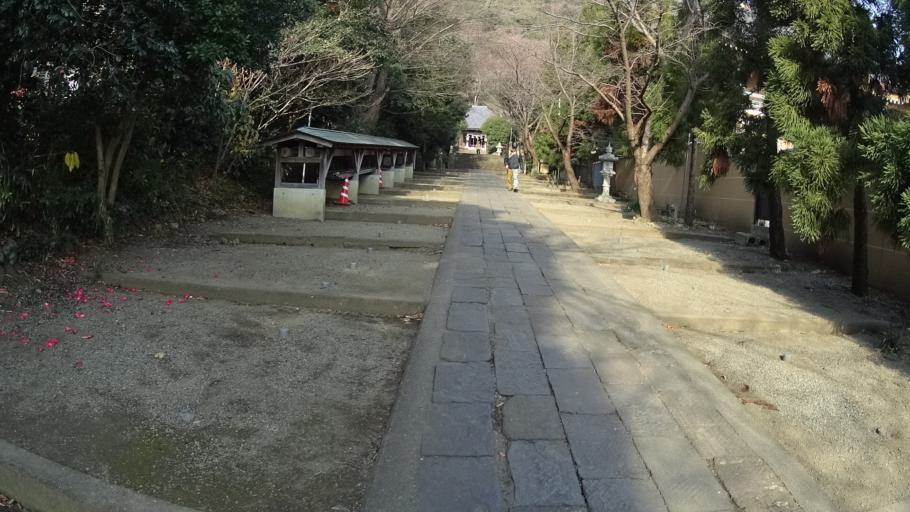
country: JP
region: Kanagawa
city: Hiratsuka
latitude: 35.3214
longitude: 139.3252
